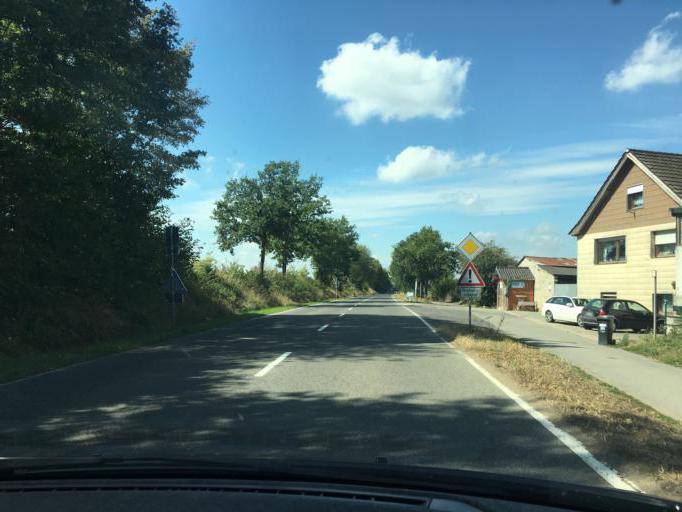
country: DE
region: North Rhine-Westphalia
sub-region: Regierungsbezirk Koln
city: Nideggen
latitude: 50.6814
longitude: 6.5162
